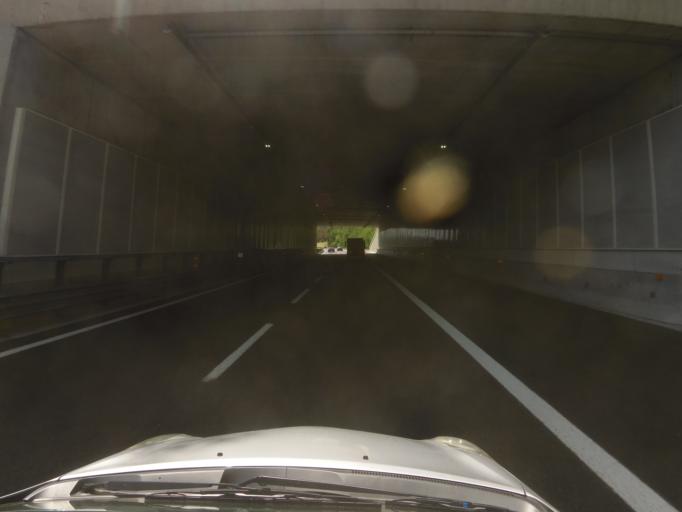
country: IT
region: Emilia-Romagna
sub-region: Provincia di Bologna
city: Grizzana
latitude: 44.2825
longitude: 11.1989
